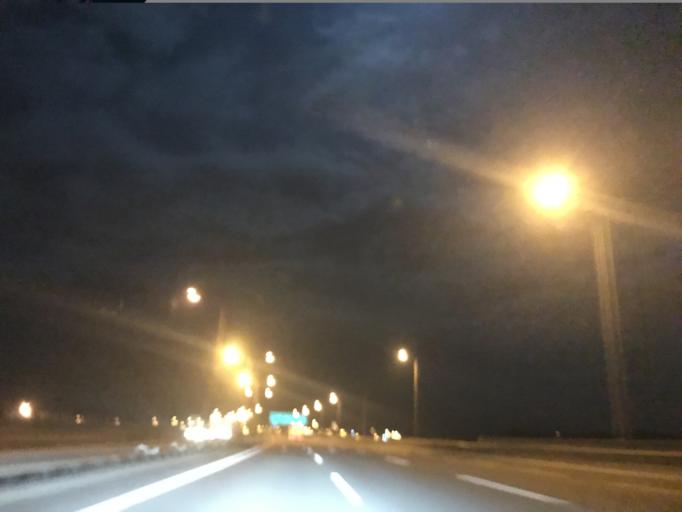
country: TR
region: Hatay
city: Mahmutlar
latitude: 36.9591
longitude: 36.1279
